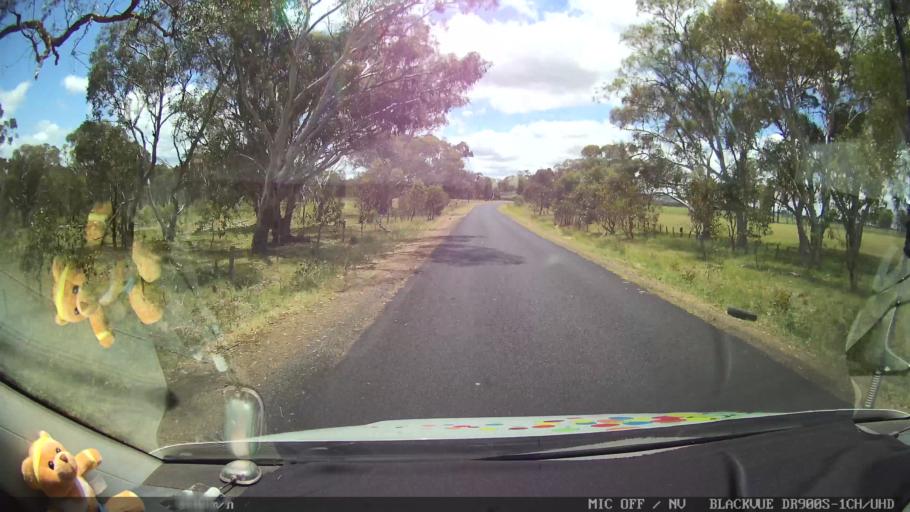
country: AU
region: New South Wales
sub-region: Glen Innes Severn
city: Glen Innes
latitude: -29.4208
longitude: 151.7145
